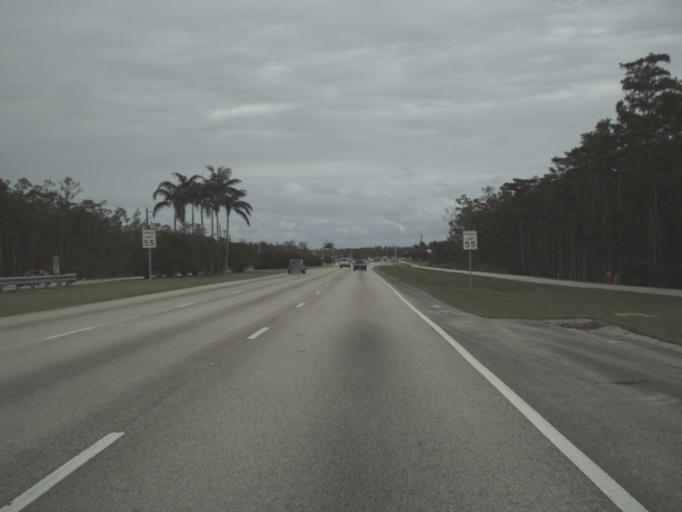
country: US
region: Florida
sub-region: Lee County
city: Fort Myers
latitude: 26.6129
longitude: -81.7908
